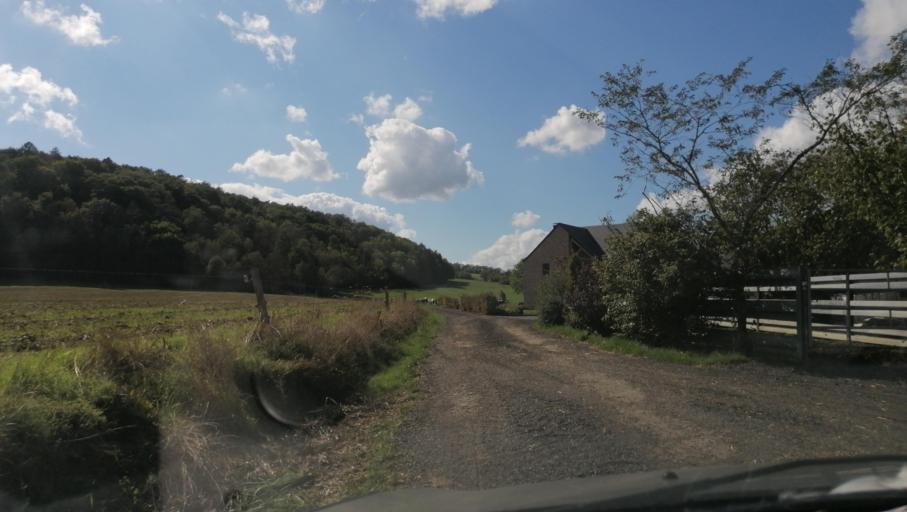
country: BE
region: Wallonia
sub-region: Province du Luxembourg
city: Tellin
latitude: 50.1243
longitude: 5.1751
